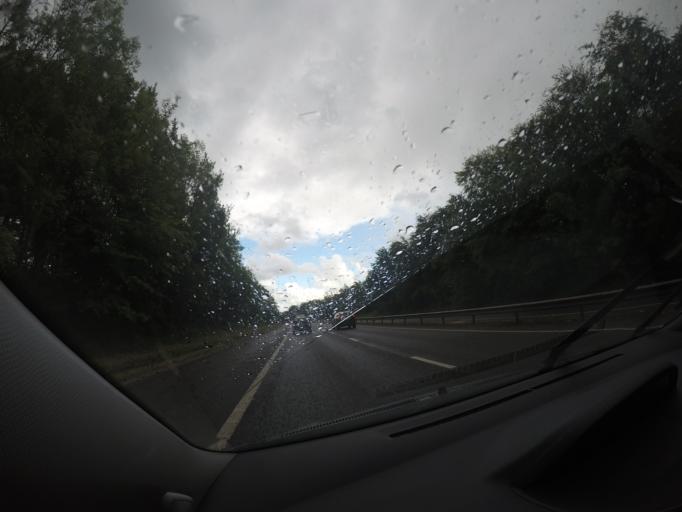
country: GB
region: Scotland
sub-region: South Lanarkshire
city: Hamilton
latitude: 55.7748
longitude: -4.0136
